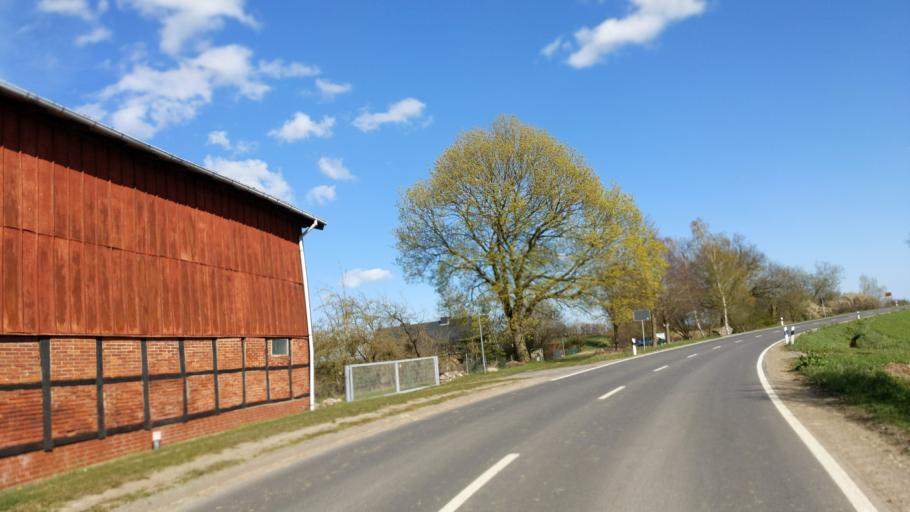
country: DE
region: Schleswig-Holstein
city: Eutin
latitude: 54.0736
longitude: 10.6320
